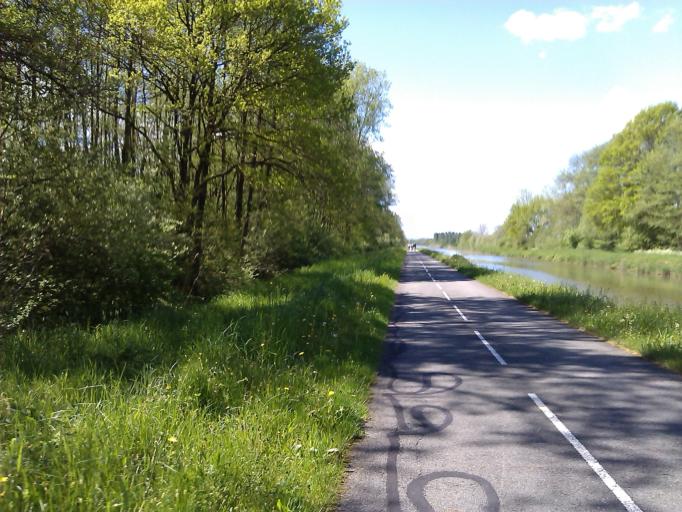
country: FR
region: Franche-Comte
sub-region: Territoire de Belfort
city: Montreux-Chateau
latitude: 47.5909
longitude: 6.9797
